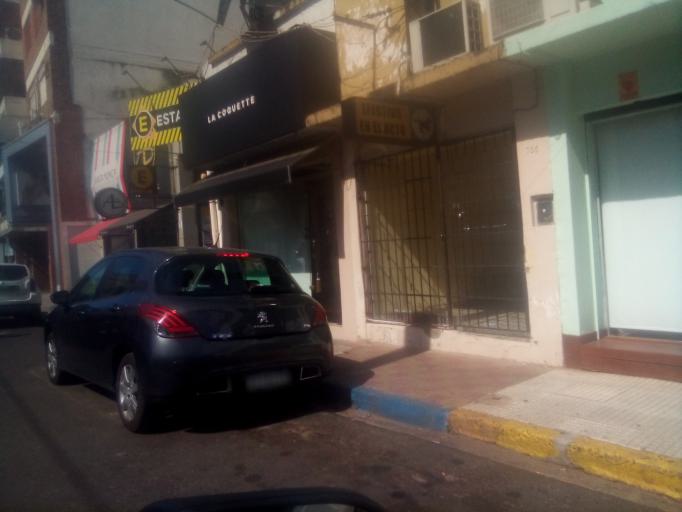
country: AR
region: Corrientes
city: Corrientes
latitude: -27.4665
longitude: -58.8355
